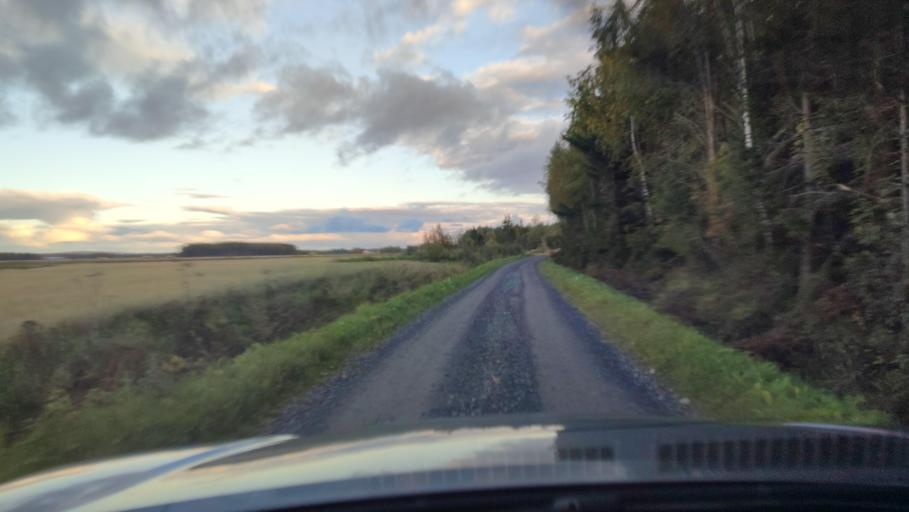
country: FI
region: Ostrobothnia
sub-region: Sydosterbotten
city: Kristinestad
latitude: 62.2517
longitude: 21.4561
